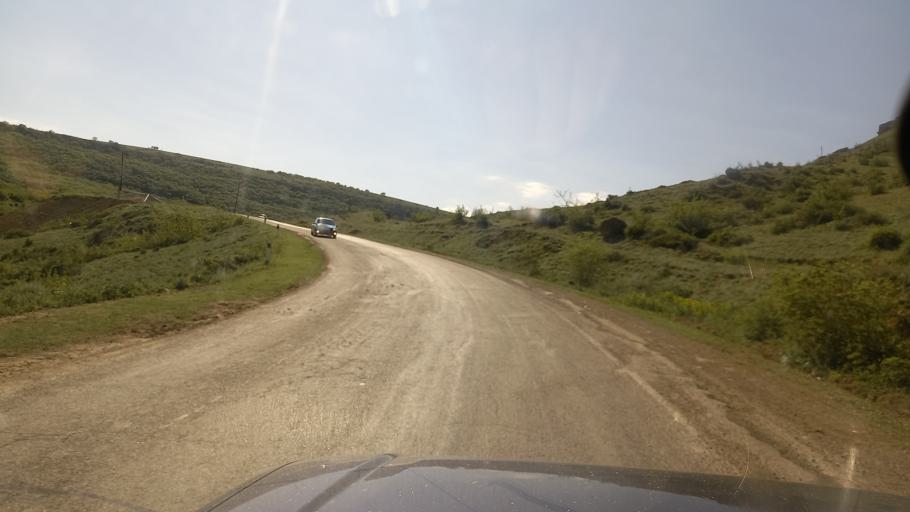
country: RU
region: Dagestan
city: Chinar
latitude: 41.9554
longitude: 48.1356
